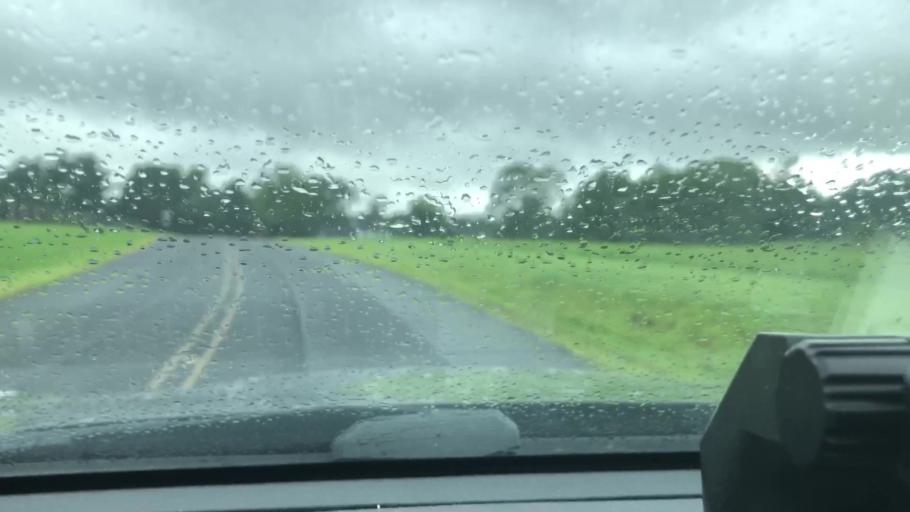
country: US
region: Pennsylvania
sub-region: Bucks County
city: Spinnerstown
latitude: 40.4648
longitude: -75.4231
